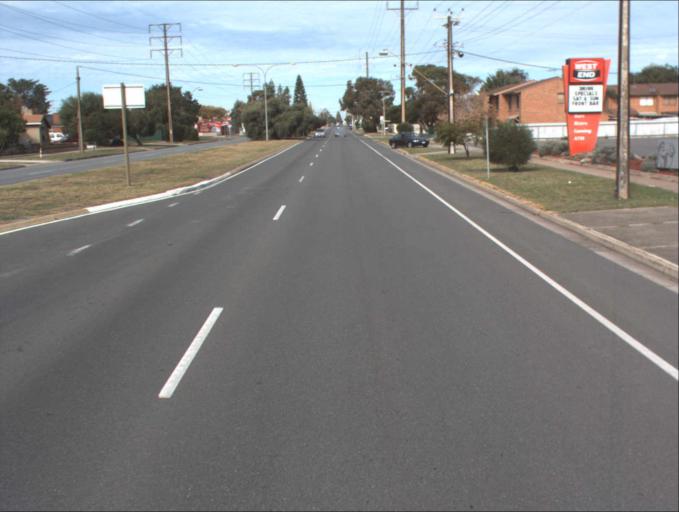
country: AU
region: South Australia
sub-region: Port Adelaide Enfield
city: Birkenhead
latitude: -34.8013
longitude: 138.5013
